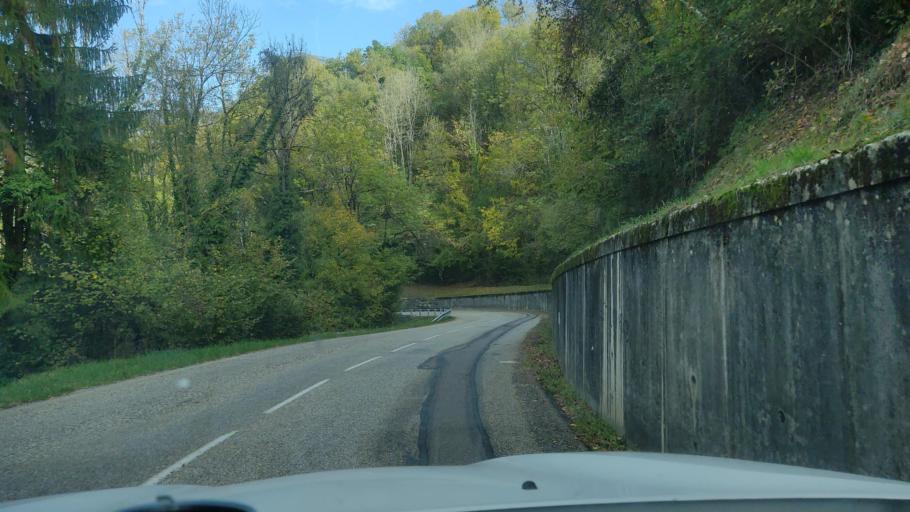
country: FR
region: Rhone-Alpes
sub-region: Departement de la Savoie
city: Barby
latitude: 45.5886
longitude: 6.0221
